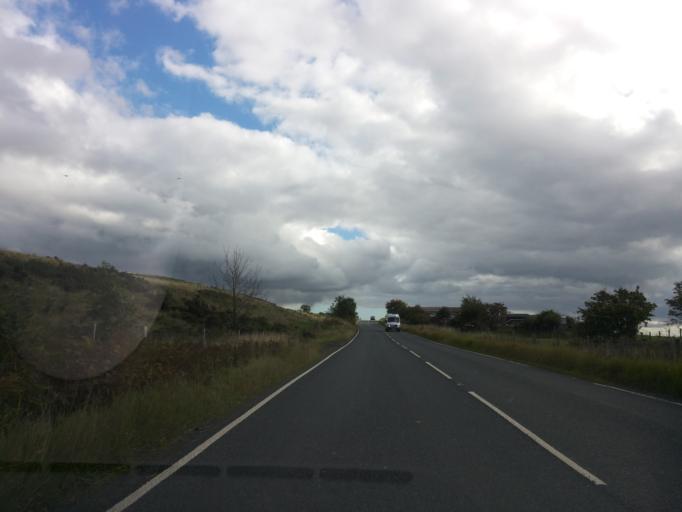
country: GB
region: England
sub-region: North Yorkshire
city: Leyburn
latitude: 54.3505
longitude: -1.8003
